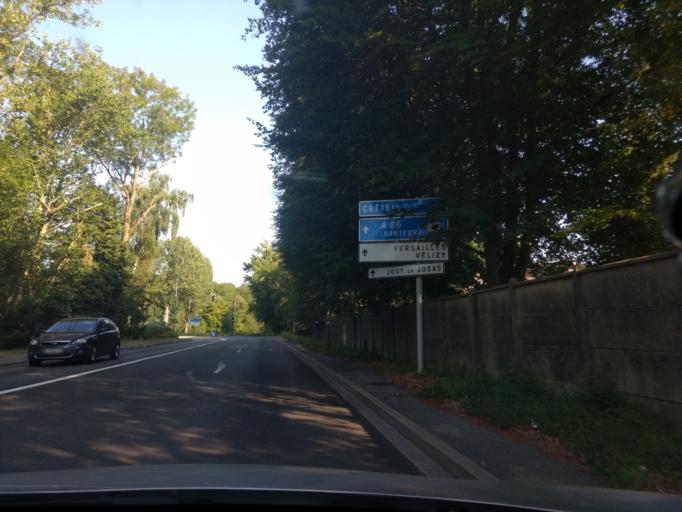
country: FR
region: Ile-de-France
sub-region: Departement des Yvelines
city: Velizy-Villacoublay
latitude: 48.7785
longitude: 2.1784
